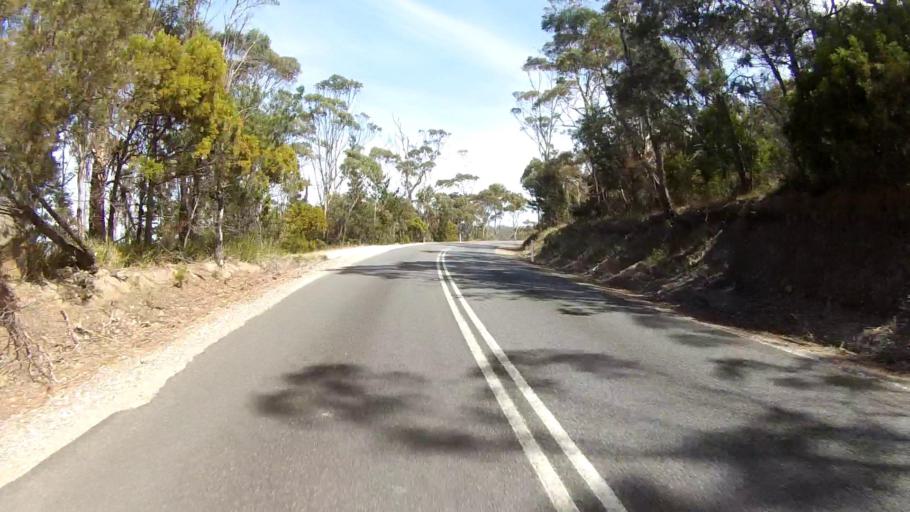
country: AU
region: Tasmania
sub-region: Huon Valley
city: Cygnet
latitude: -43.2673
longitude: 147.1450
